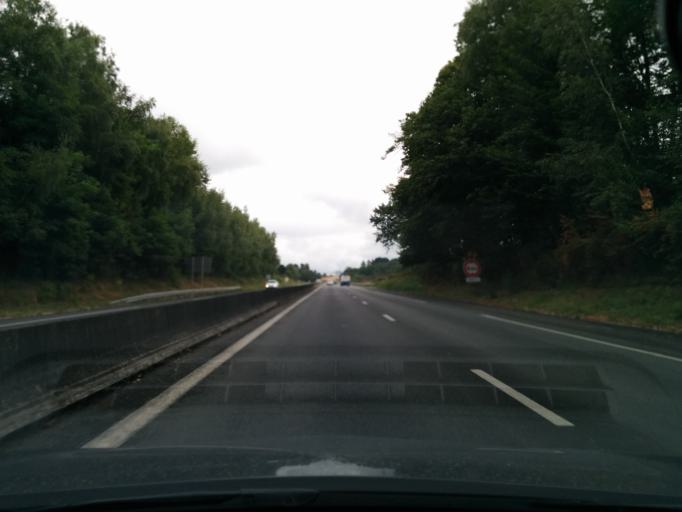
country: FR
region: Limousin
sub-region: Departement de la Correze
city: Donzenac
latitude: 45.2475
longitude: 1.5290
